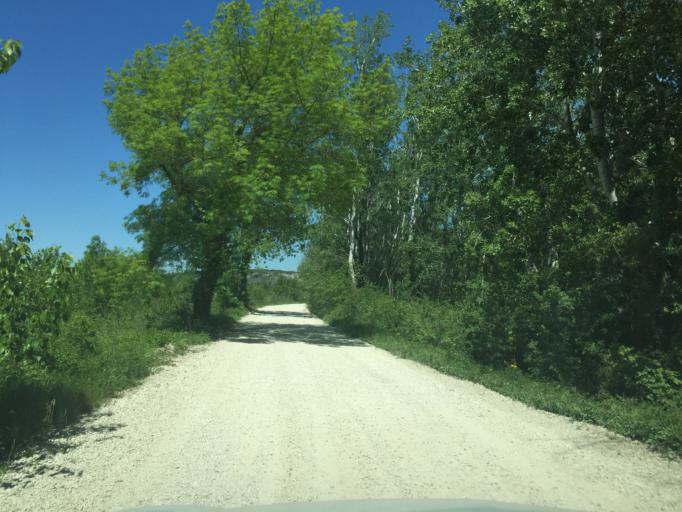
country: FR
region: Languedoc-Roussillon
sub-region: Departement du Gard
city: Roquemaure
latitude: 44.0566
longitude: 4.7945
